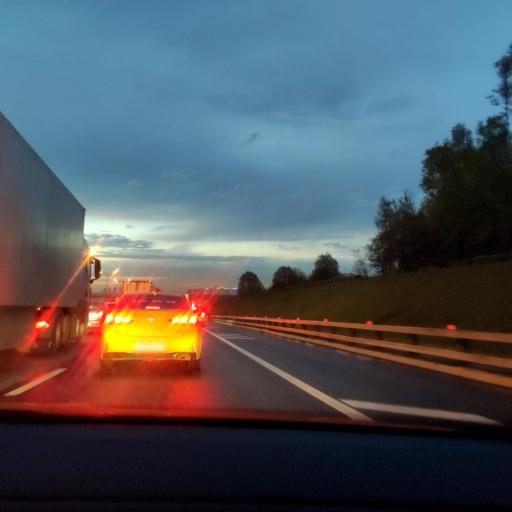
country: RU
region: Moscow
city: Rublevo
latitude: 55.7579
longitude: 37.3709
